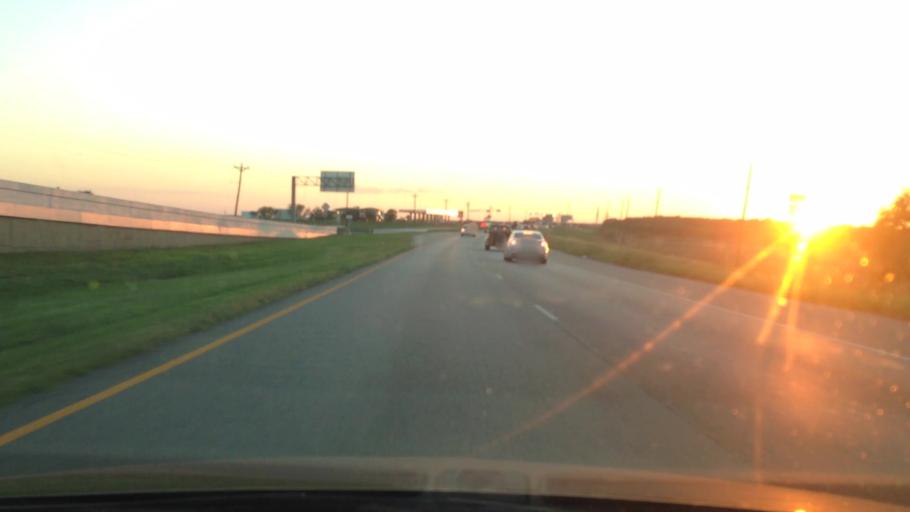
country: US
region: Texas
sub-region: Denton County
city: The Colony
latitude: 33.0507
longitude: -96.9235
